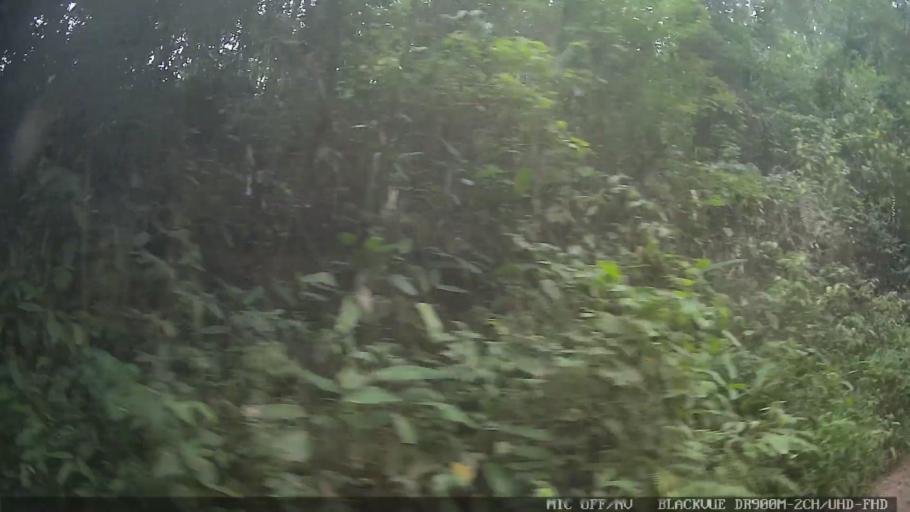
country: BR
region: Sao Paulo
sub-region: Bom Jesus Dos Perdoes
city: Bom Jesus dos Perdoes
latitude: -23.1523
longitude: -46.5099
